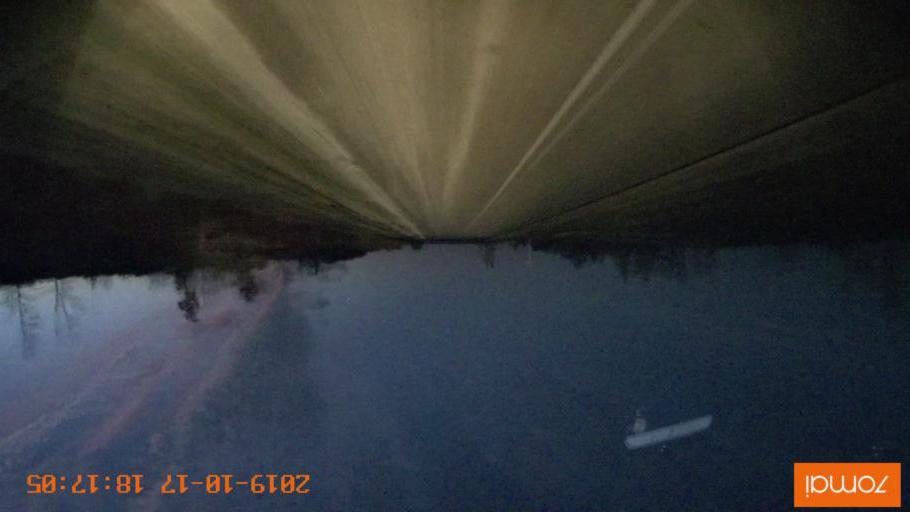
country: RU
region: Tula
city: Kurkino
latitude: 53.3938
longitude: 38.5075
